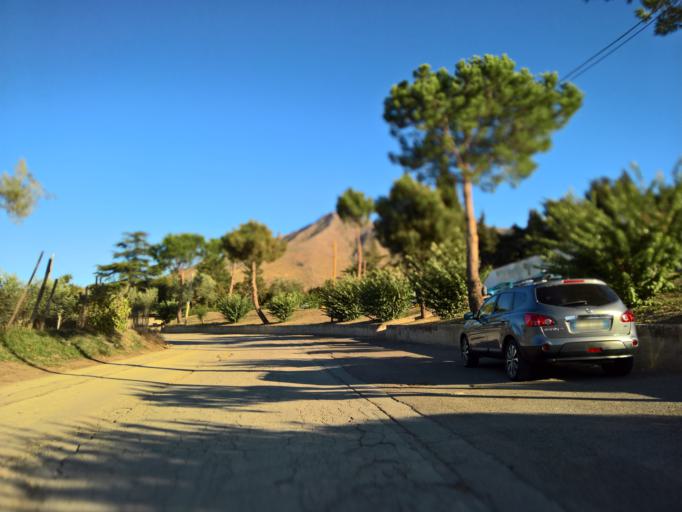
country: IT
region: Campania
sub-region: Provincia di Caserta
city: San Prisco
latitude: 41.0939
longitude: 14.2783
